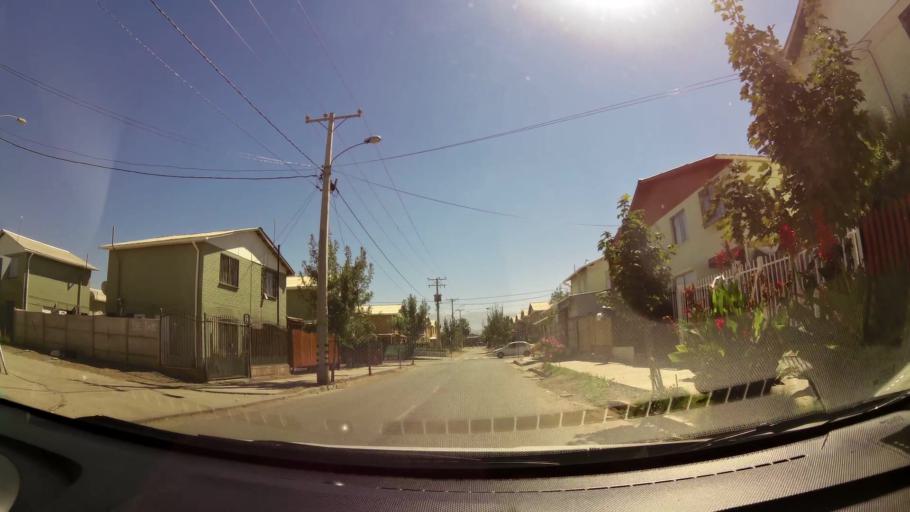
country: CL
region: O'Higgins
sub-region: Provincia de Cachapoal
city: Rancagua
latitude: -34.1663
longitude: -70.6988
